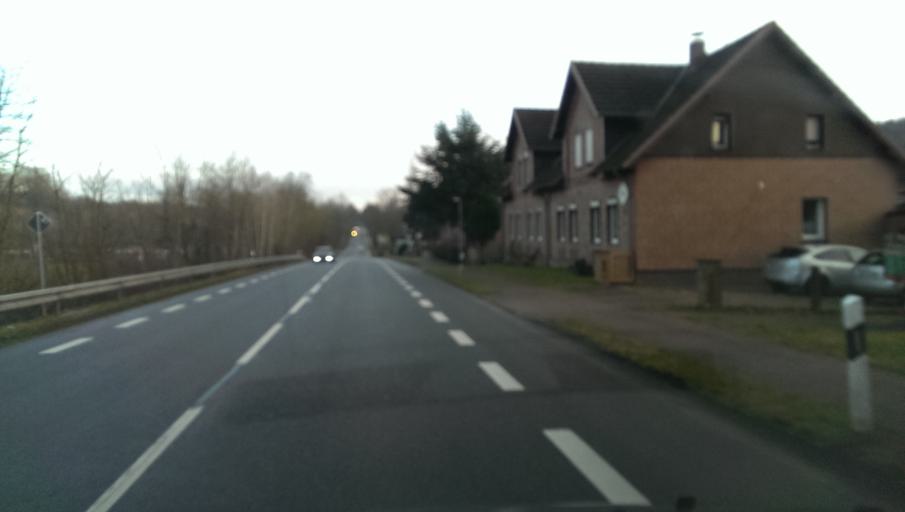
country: DE
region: Lower Saxony
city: Lenne
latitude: 51.8964
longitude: 9.6991
